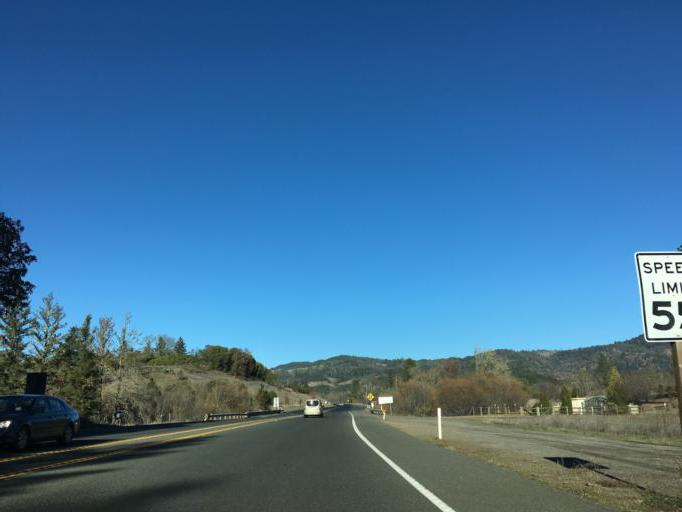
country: US
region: California
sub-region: Mendocino County
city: Laytonville
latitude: 39.6238
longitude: -123.4645
